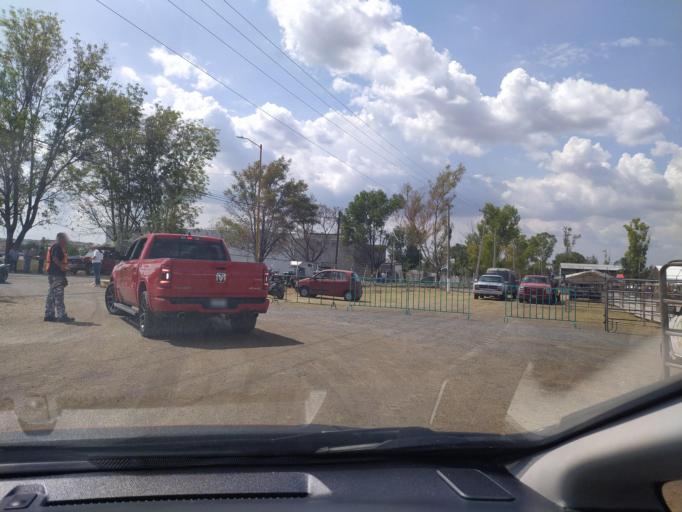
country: MX
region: Guanajuato
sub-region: San Francisco del Rincon
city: Estacion de San Francisco
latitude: 21.0295
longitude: -101.8394
